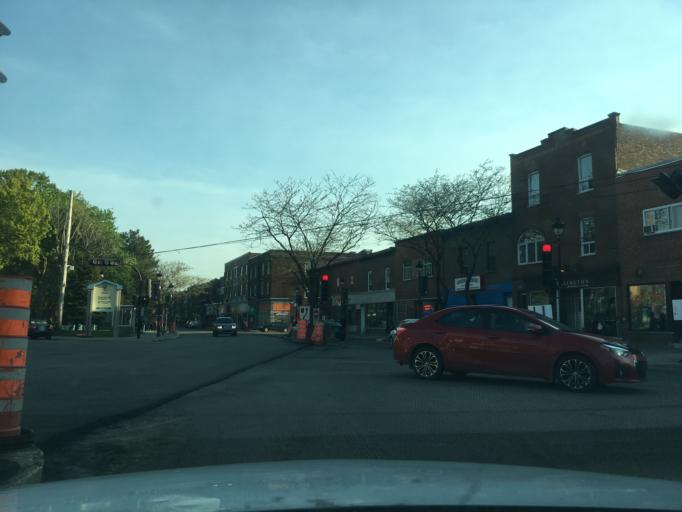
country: CA
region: Quebec
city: Westmount
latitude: 45.4679
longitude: -73.5664
